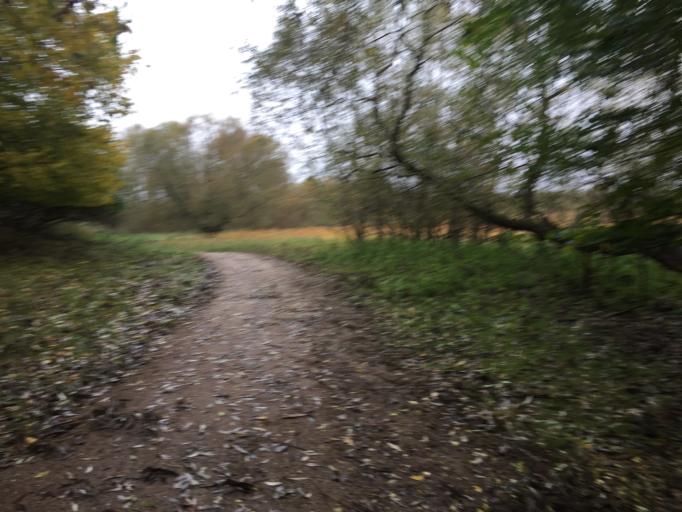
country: DK
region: Zealand
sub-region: Ringsted Kommune
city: Ringsted
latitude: 55.4851
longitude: 11.7504
